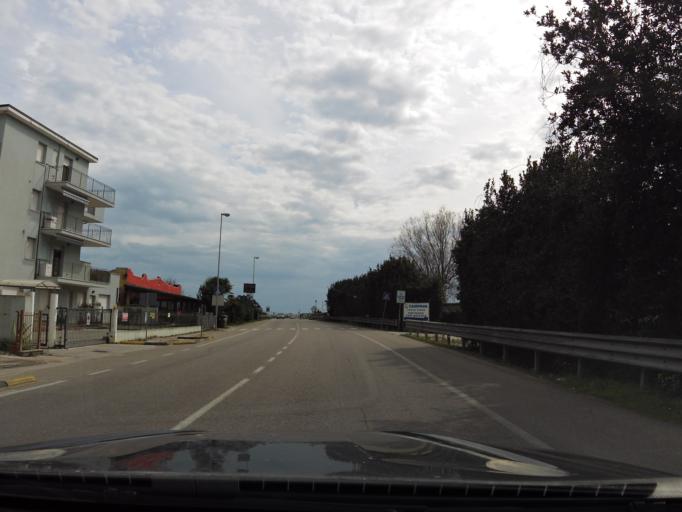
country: IT
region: The Marches
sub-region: Provincia di Macerata
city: Porto Potenza Picena
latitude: 43.3491
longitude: 13.7016
